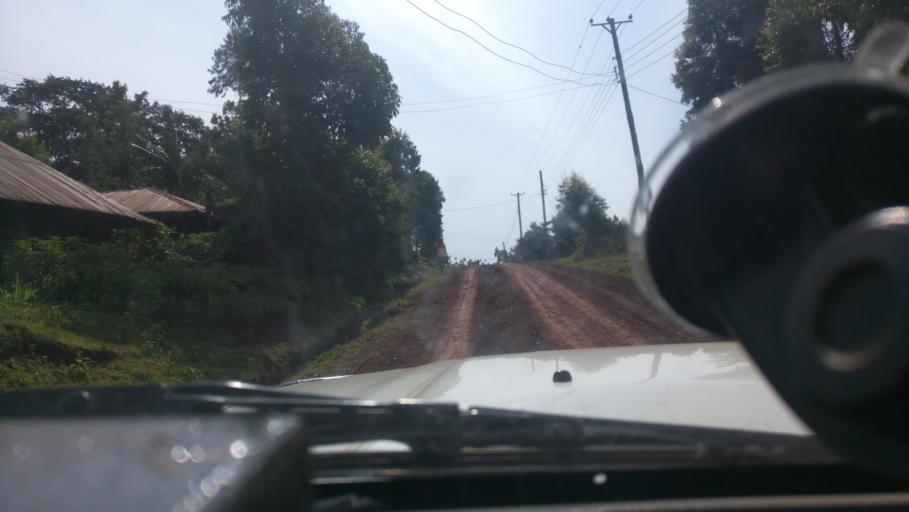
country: KE
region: Nyamira District
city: Nyamira
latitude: -0.5575
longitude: 34.9533
